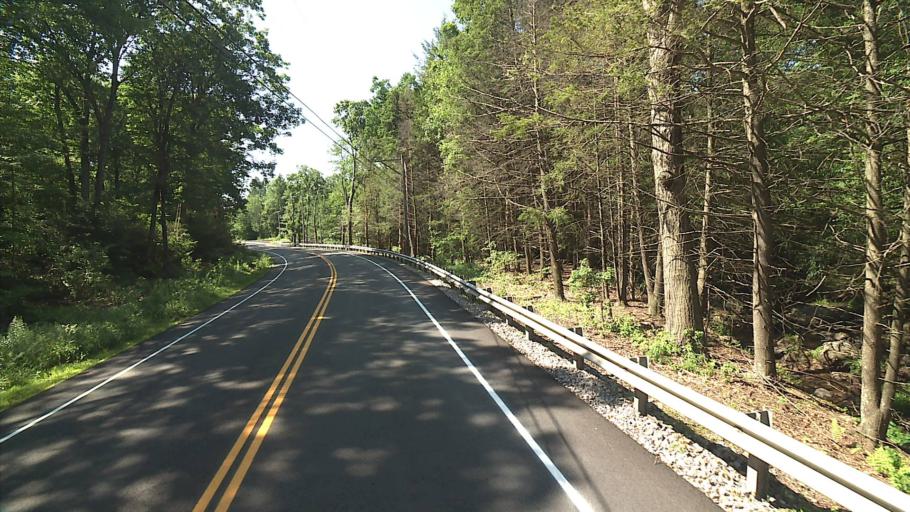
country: US
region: Connecticut
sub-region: Litchfield County
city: Terryville
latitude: 41.7185
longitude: -73.0132
